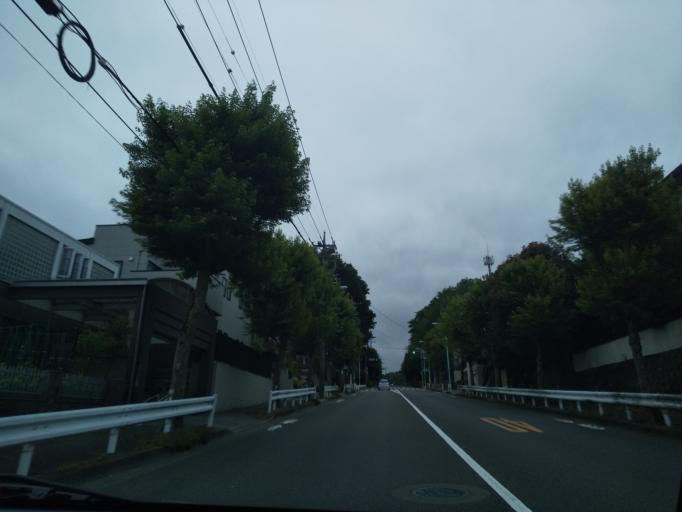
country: JP
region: Tokyo
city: Hino
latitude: 35.6454
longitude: 139.3912
